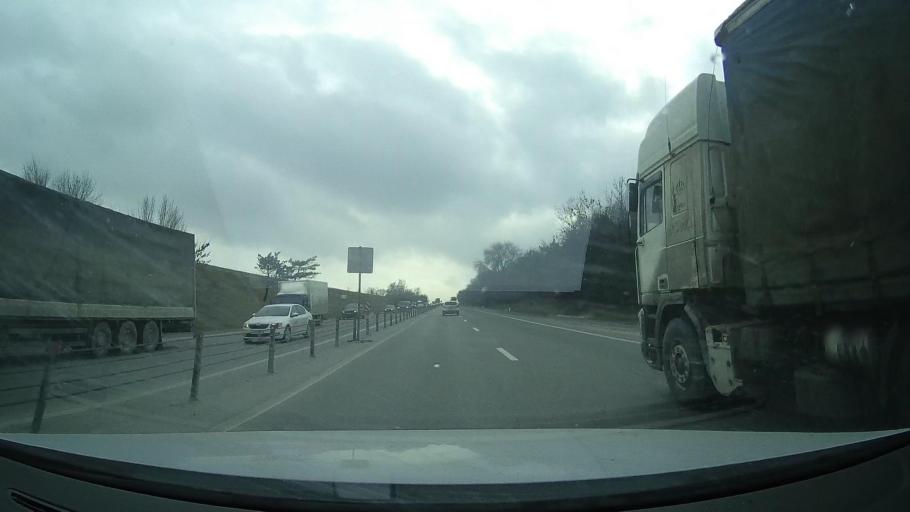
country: RU
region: Rostov
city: Grushevskaya
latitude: 47.4318
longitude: 39.9749
